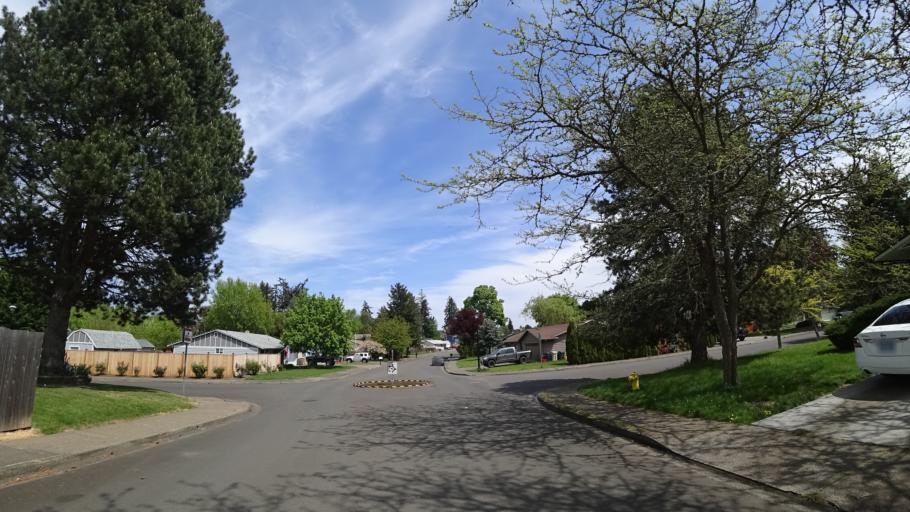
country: US
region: Oregon
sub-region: Washington County
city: Aloha
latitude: 45.4738
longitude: -122.8864
